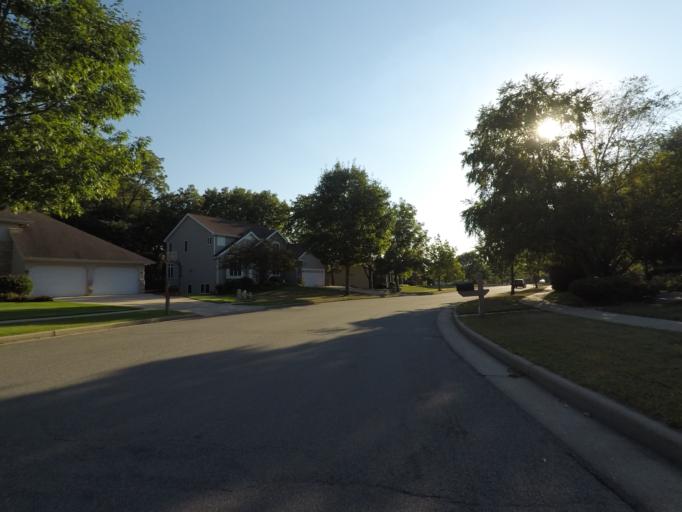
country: US
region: Wisconsin
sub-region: Dane County
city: Verona
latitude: 43.0056
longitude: -89.5380
